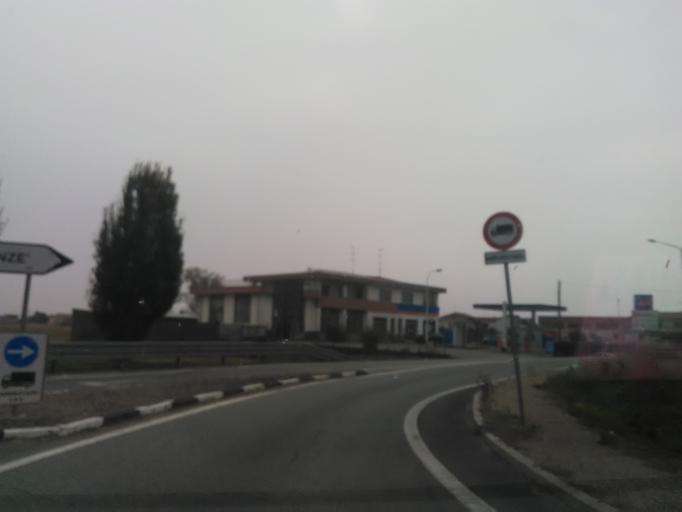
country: IT
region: Piedmont
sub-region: Provincia di Vercelli
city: Bianze
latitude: 45.3126
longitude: 8.1270
